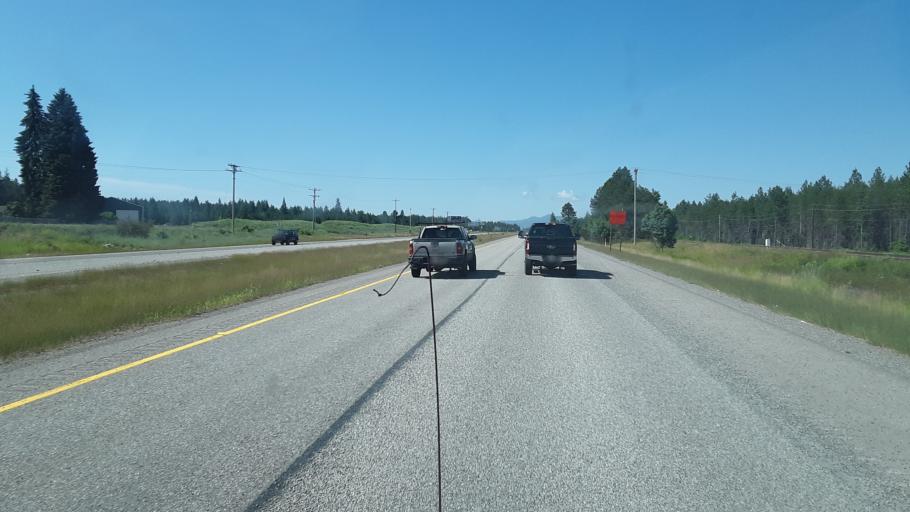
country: US
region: Idaho
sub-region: Kootenai County
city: Hayden
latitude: 47.8442
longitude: -116.7656
